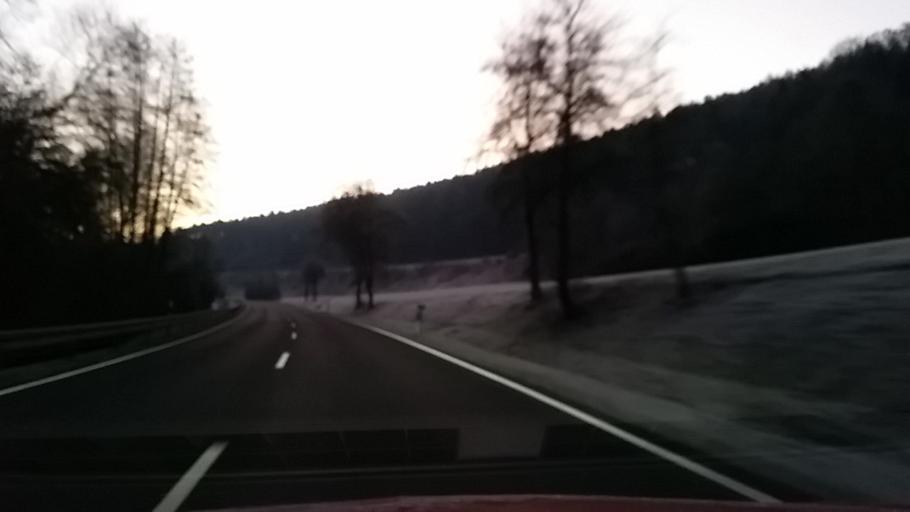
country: DE
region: Bavaria
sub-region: Regierungsbezirk Unterfranken
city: Thungen
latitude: 49.9401
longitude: 9.8442
